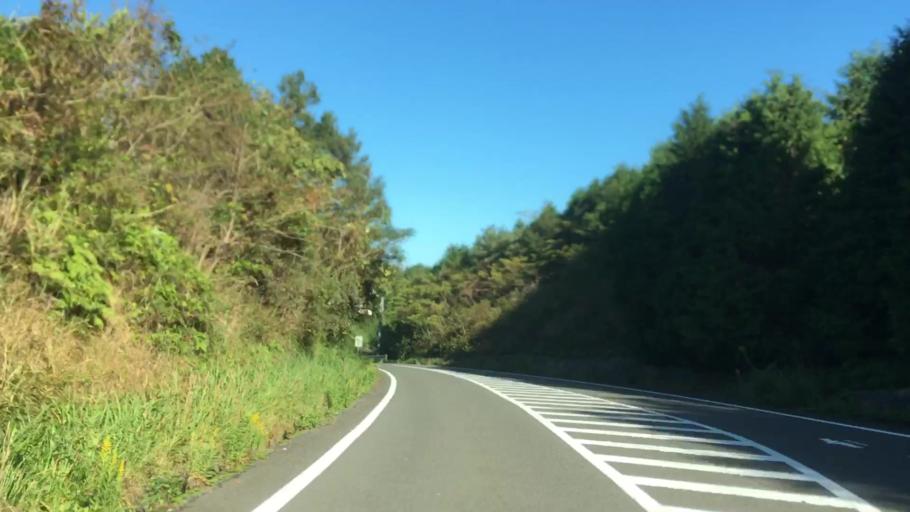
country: JP
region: Nagasaki
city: Sasebo
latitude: 33.0152
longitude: 129.7062
